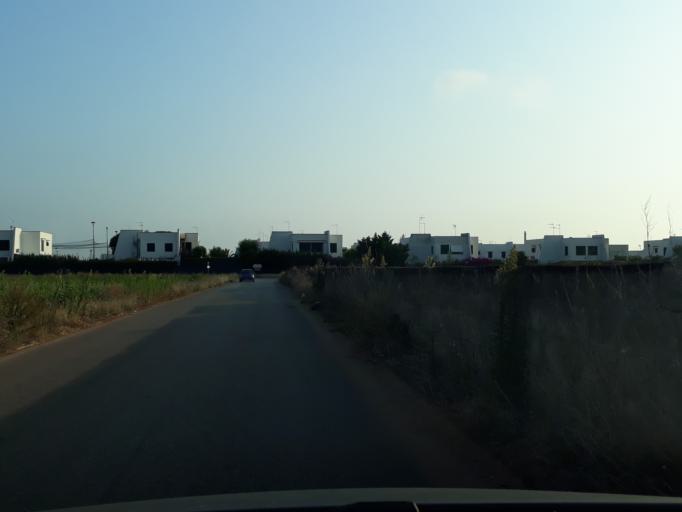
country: IT
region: Apulia
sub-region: Provincia di Brindisi
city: Carovigno
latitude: 40.7510
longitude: 17.7081
